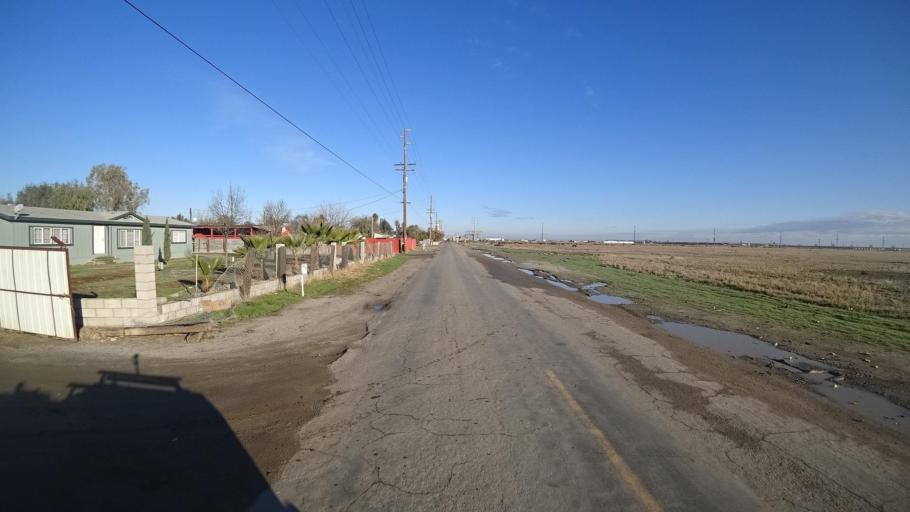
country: US
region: California
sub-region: Kern County
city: Delano
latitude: 35.7878
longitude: -119.2944
